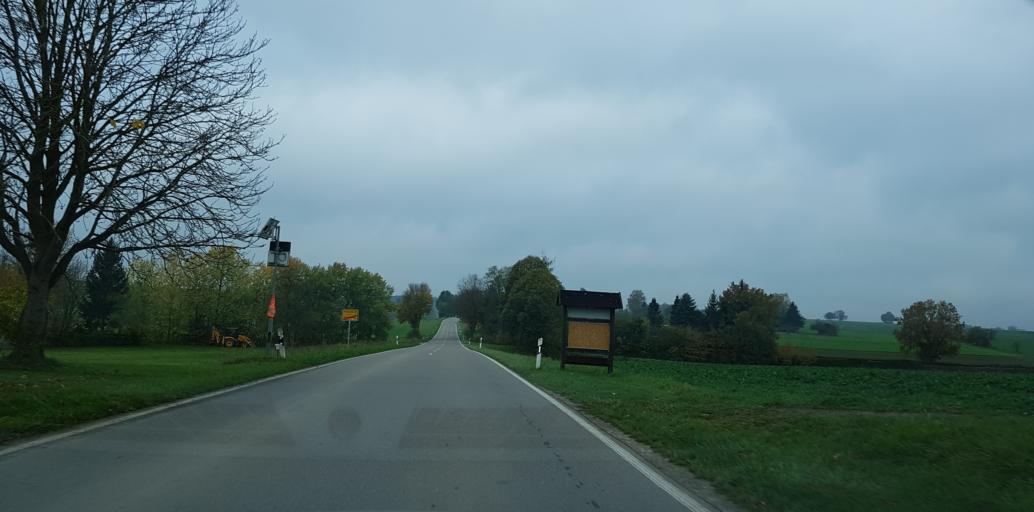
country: DE
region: Baden-Wuerttemberg
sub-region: Tuebingen Region
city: Oberdischingen
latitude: 48.3041
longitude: 9.8263
